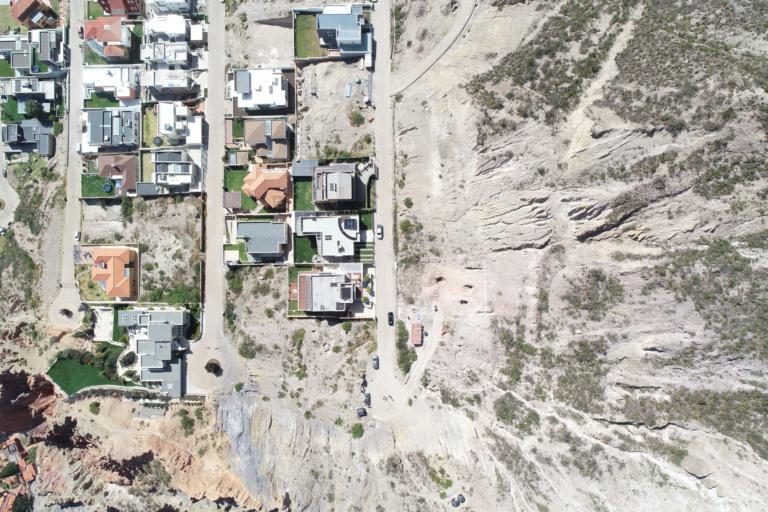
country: BO
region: La Paz
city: La Paz
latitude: -16.5554
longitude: -68.0822
